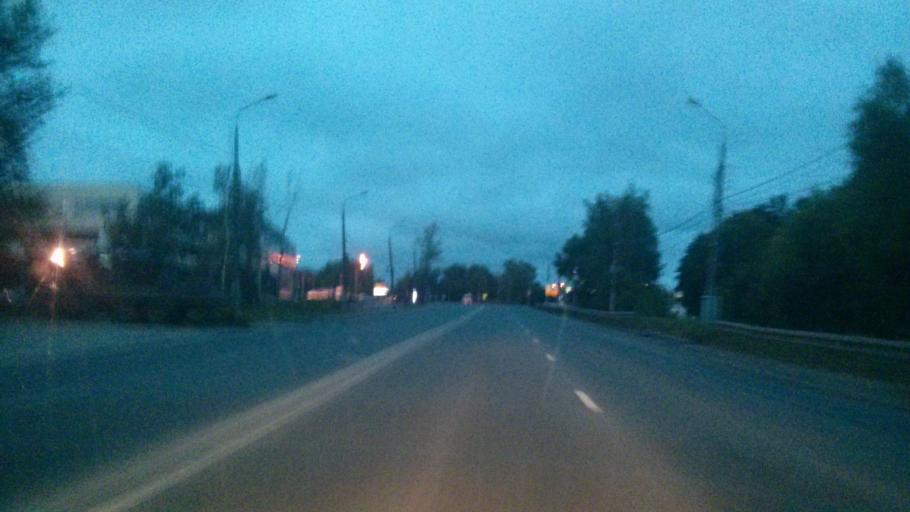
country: RU
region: Nizjnij Novgorod
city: Nizhniy Novgorod
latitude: 56.2275
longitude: 43.9425
